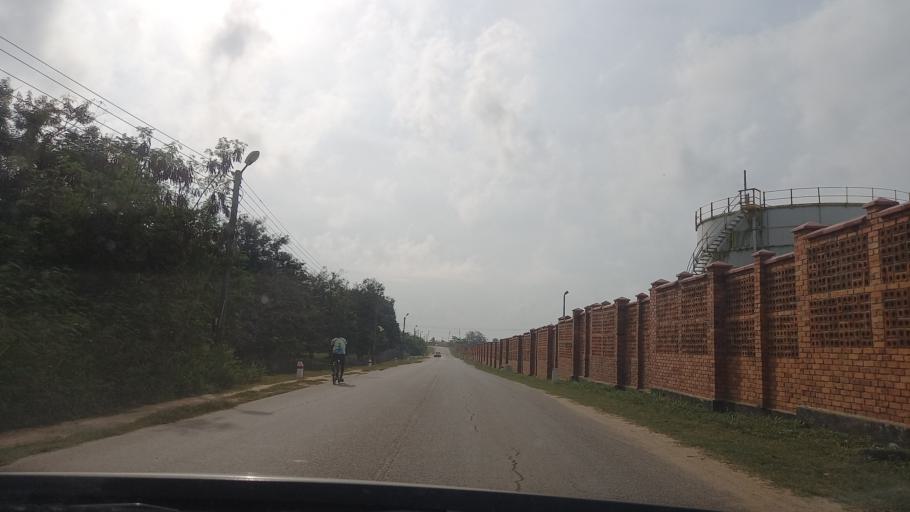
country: GH
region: Western
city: Shama Junction
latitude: 4.9762
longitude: -1.6582
